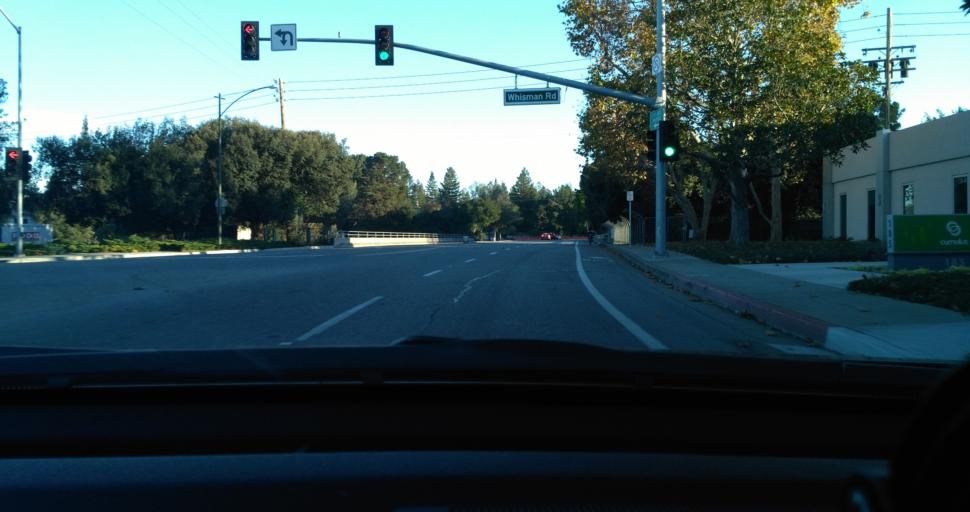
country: US
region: California
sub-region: Santa Clara County
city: Mountain View
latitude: 37.3864
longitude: -122.0653
